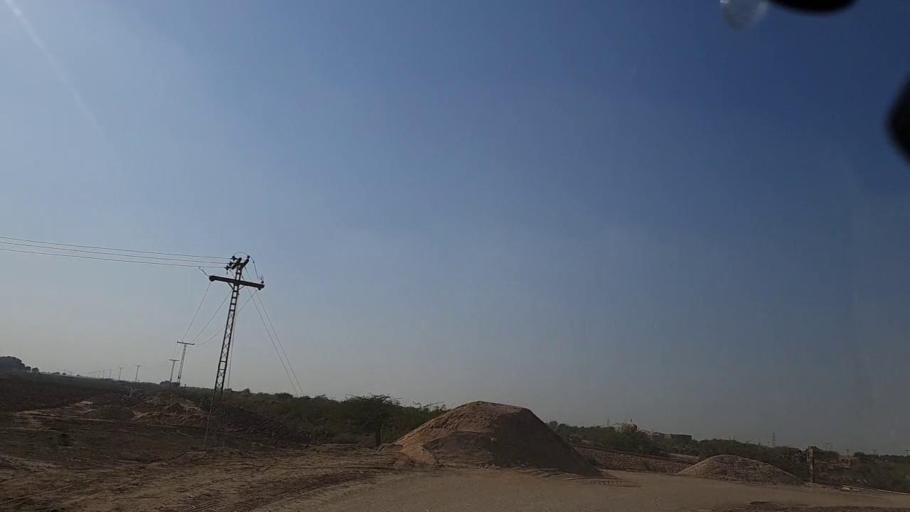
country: PK
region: Sindh
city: Mirpur Khas
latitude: 25.5127
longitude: 68.9302
